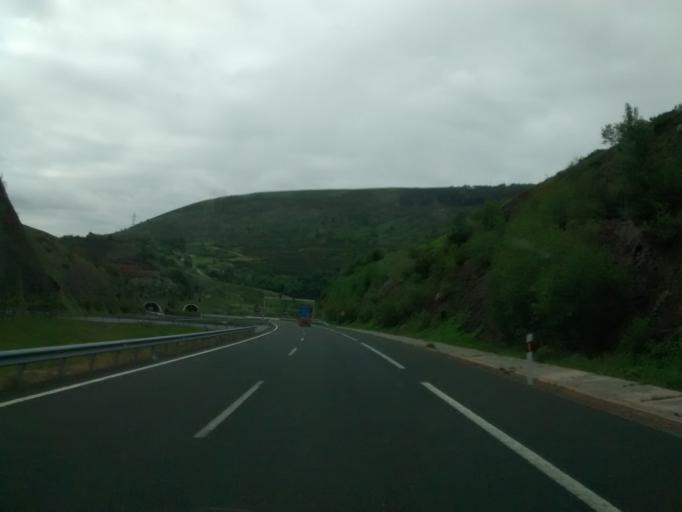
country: ES
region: Cantabria
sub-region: Provincia de Cantabria
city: Los Corrales de Buelna
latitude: 43.2215
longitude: -4.0784
